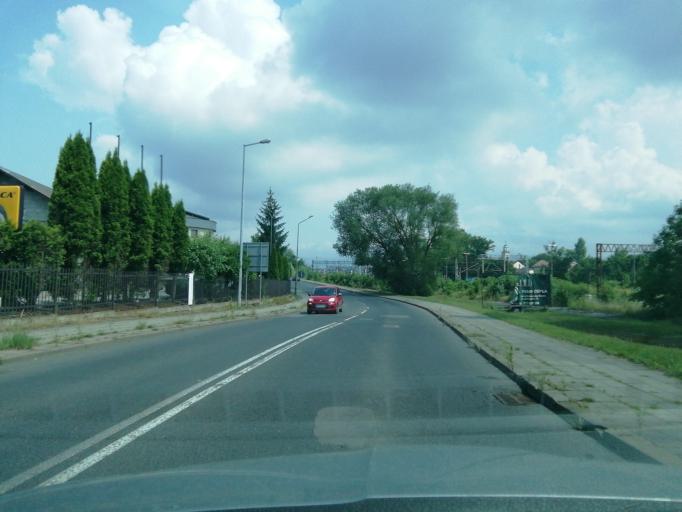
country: PL
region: Silesian Voivodeship
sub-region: Powiat zywiecki
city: Zywiec
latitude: 49.6744
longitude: 19.1829
